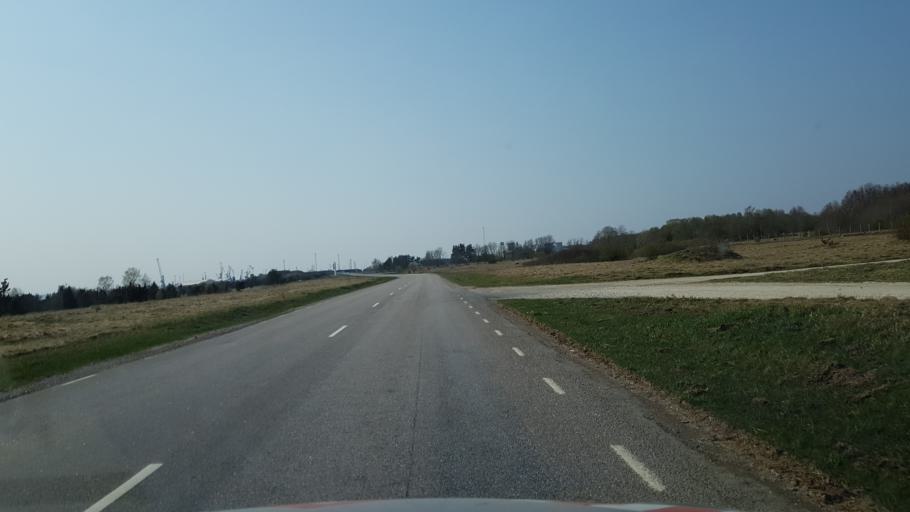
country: EE
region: Harju
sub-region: Paldiski linn
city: Paldiski
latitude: 59.3295
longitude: 24.1079
